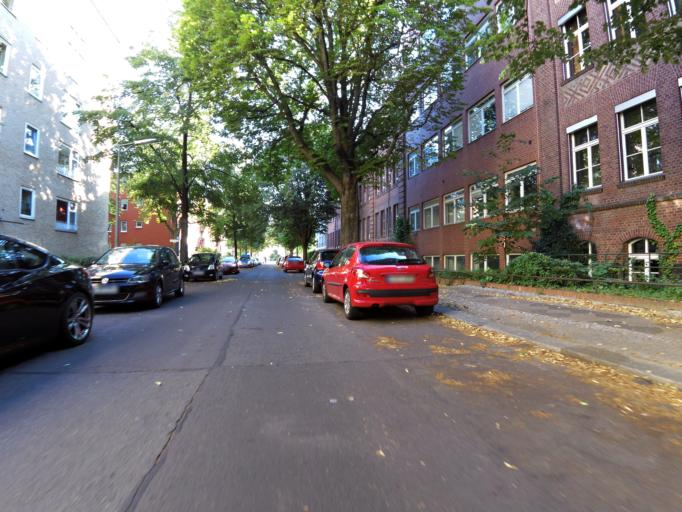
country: DE
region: Berlin
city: Steglitz Bezirk
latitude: 52.4527
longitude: 13.3360
